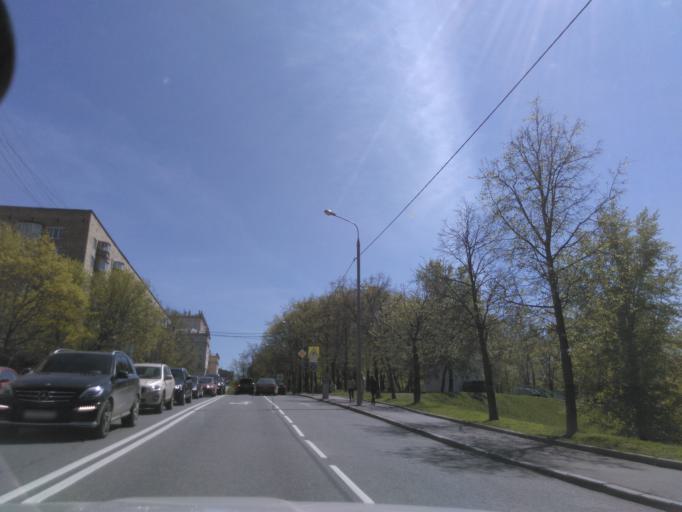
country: RU
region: Moscow
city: Luzhniki
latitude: 55.7289
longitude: 37.5584
